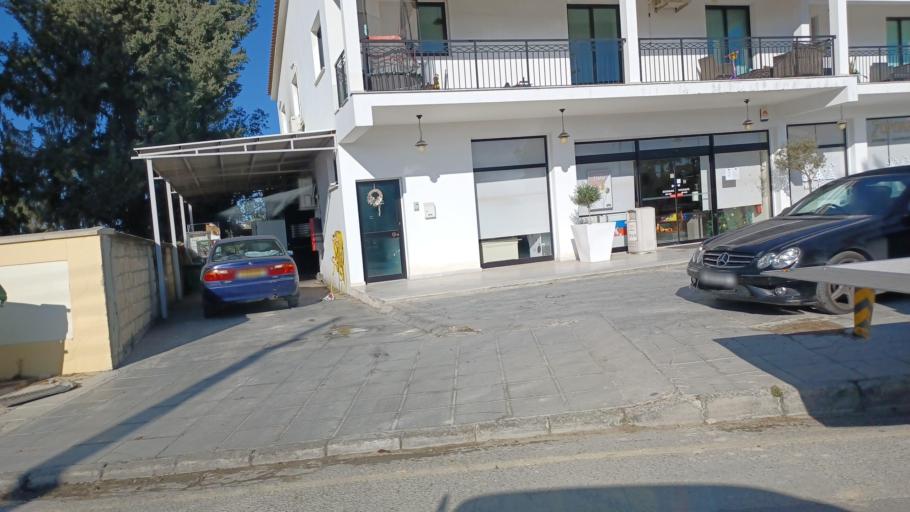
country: CY
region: Larnaka
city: Athienou
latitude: 35.0586
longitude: 33.5363
